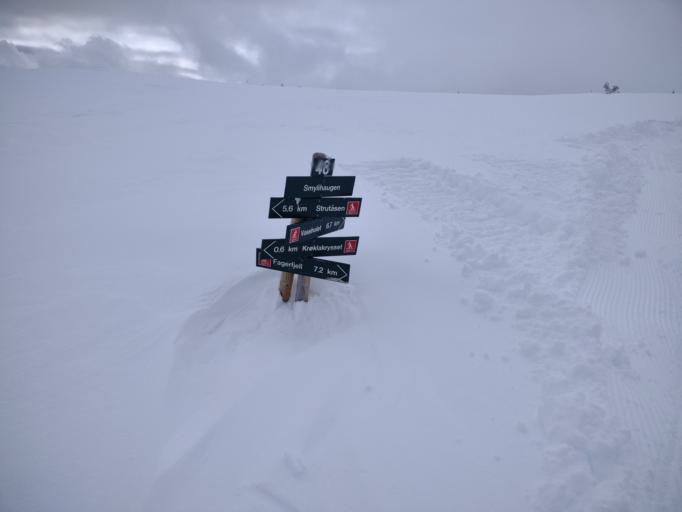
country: NO
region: Buskerud
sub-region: Rollag
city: Rollag
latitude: 59.7978
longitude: 9.3016
